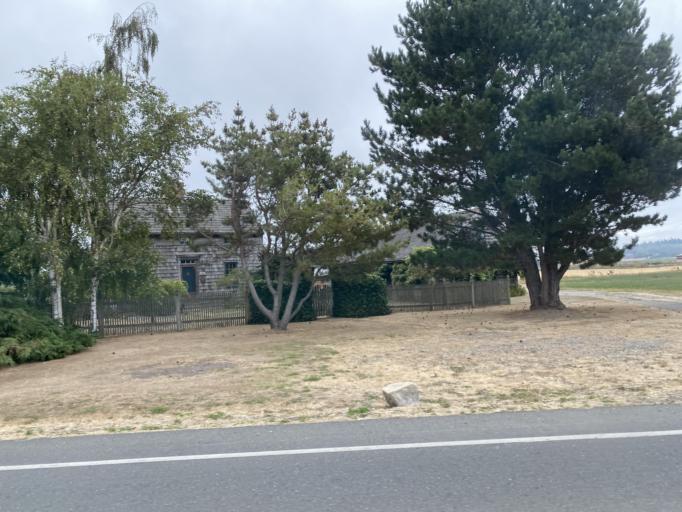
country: US
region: Washington
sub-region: Island County
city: Coupeville
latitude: 48.2043
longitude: -122.6934
